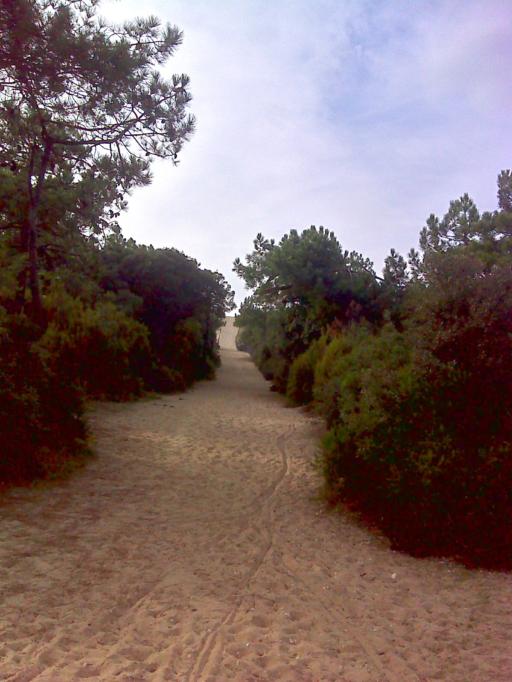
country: FR
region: Poitou-Charentes
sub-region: Departement de la Charente-Maritime
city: Les Mathes
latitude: 45.7058
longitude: -1.2330
